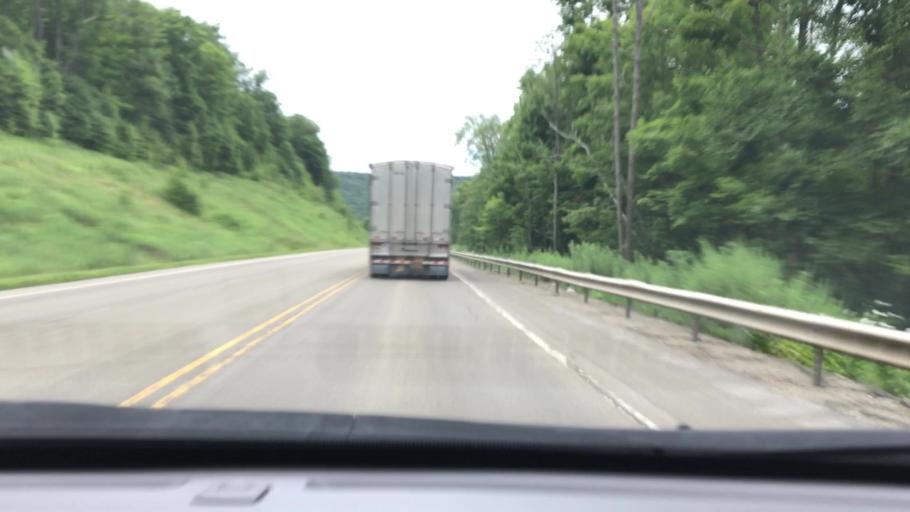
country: US
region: Pennsylvania
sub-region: McKean County
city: Kane
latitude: 41.7559
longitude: -78.6969
